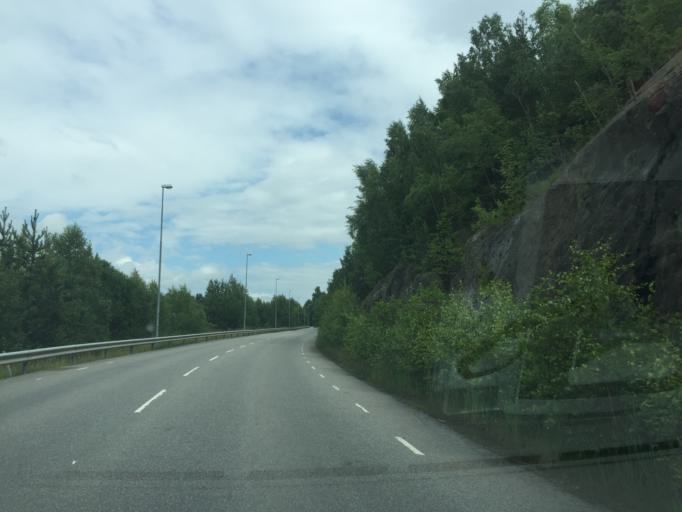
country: SE
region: Stockholm
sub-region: Botkyrka Kommun
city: Tumba
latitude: 59.1986
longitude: 17.8635
